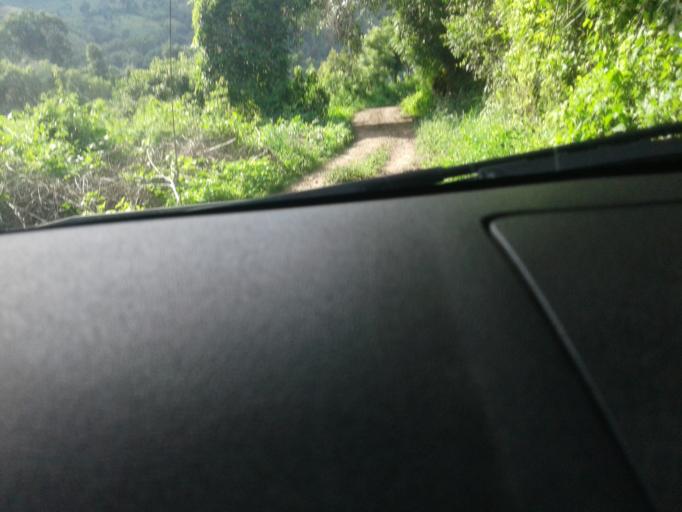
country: NI
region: Matagalpa
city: Terrabona
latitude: 12.7891
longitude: -85.9831
